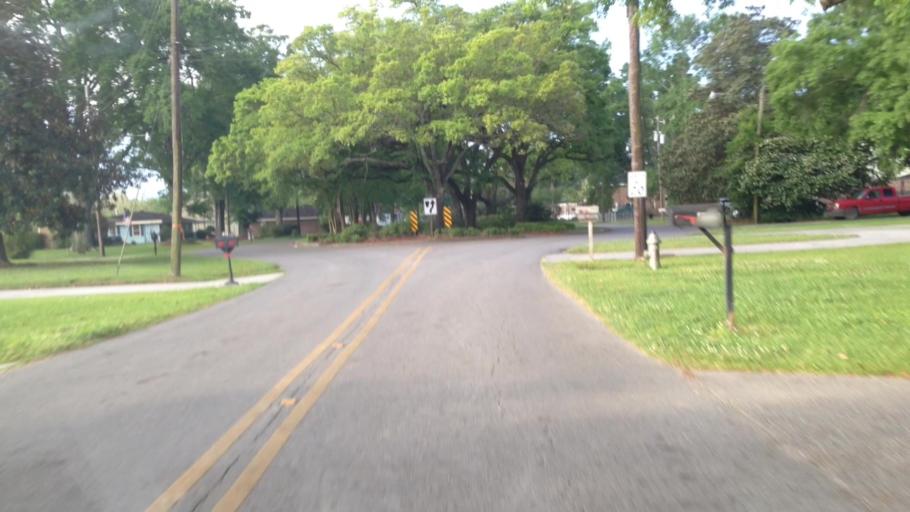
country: US
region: Louisiana
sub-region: Jefferson Parish
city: Bridge City
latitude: 29.9451
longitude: -90.1530
